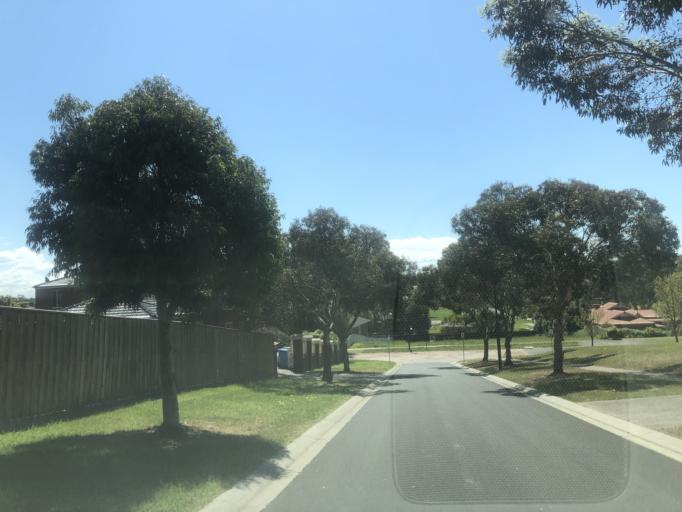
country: AU
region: Victoria
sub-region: Casey
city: Endeavour Hills
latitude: -37.9911
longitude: 145.2799
